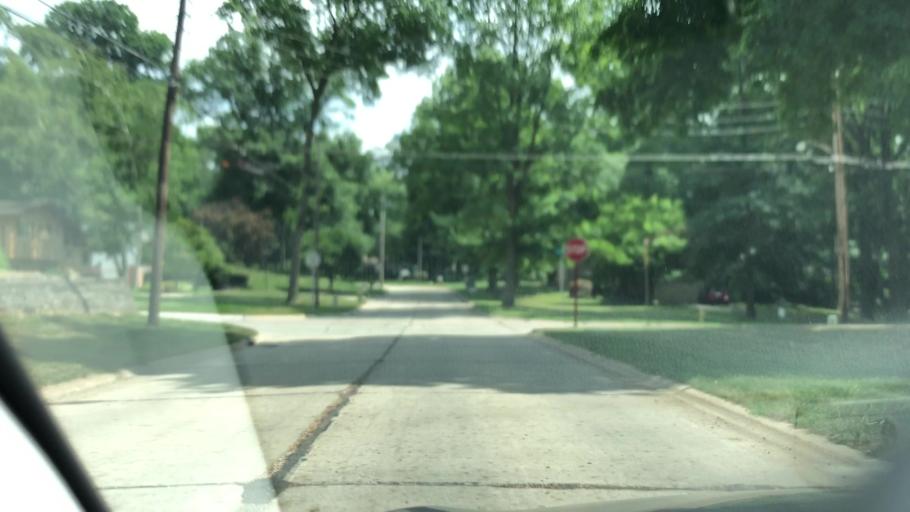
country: US
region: Ohio
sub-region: Summit County
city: Fairlawn
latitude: 41.1260
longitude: -81.6214
